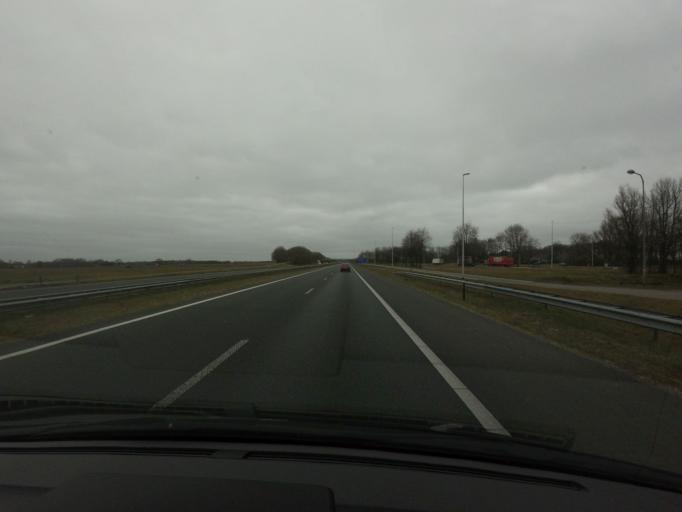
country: NL
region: Groningen
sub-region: Gemeente Hoogezand-Sappemeer
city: Hoogezand
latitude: 53.1872
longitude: 6.7158
